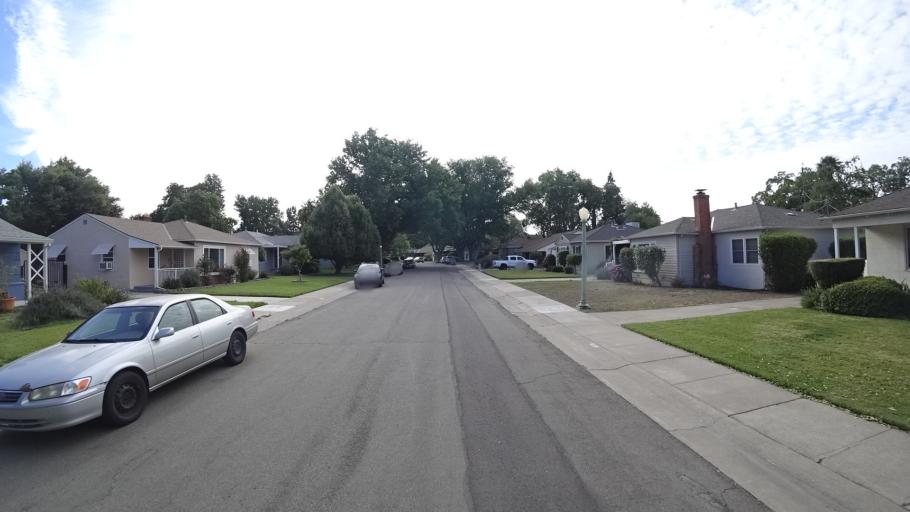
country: US
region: California
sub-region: Sacramento County
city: Sacramento
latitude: 38.5596
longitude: -121.5081
